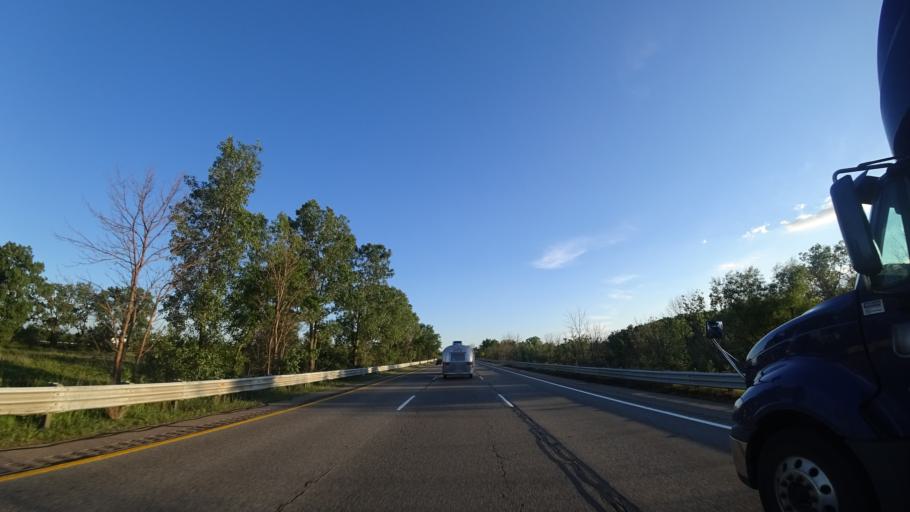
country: US
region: Michigan
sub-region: Berrien County
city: New Buffalo
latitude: 41.8044
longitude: -86.7041
